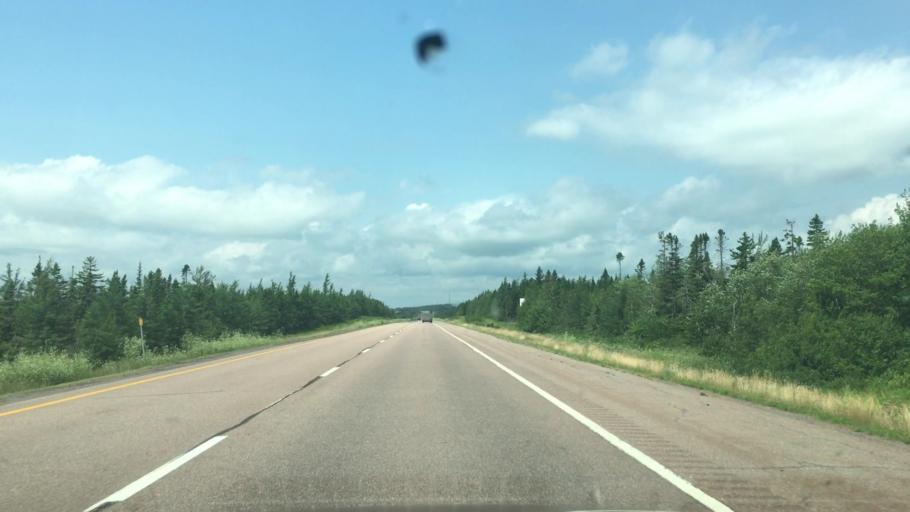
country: CA
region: New Brunswick
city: Sackville
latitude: 45.9812
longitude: -64.4622
